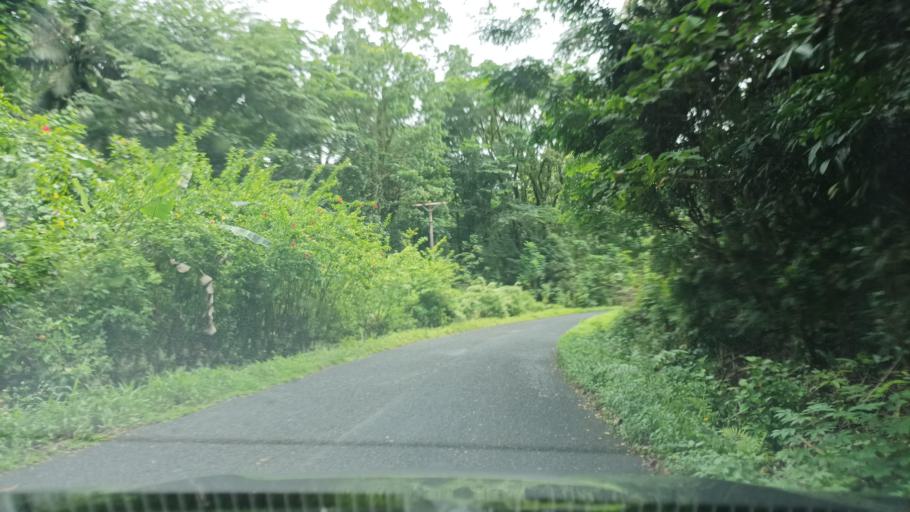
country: FM
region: Pohnpei
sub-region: Madolenihm Municipality
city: Madolenihm Municipality Government
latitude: 6.8416
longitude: 158.3001
